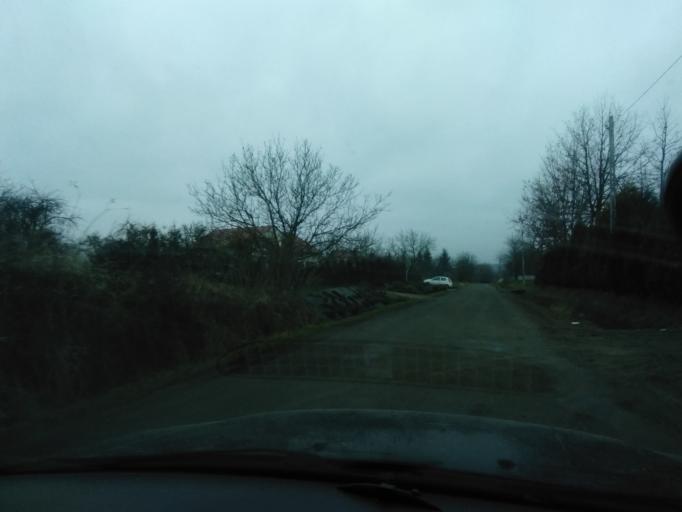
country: PL
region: Subcarpathian Voivodeship
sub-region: Powiat jaroslawski
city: Pruchnik
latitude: 49.9226
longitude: 22.5350
